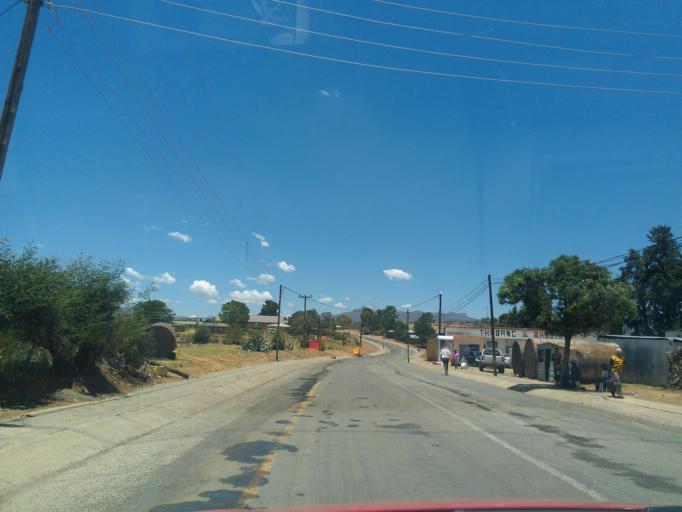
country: LS
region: Berea
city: Teyateyaneng
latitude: -29.1112
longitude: 27.9666
